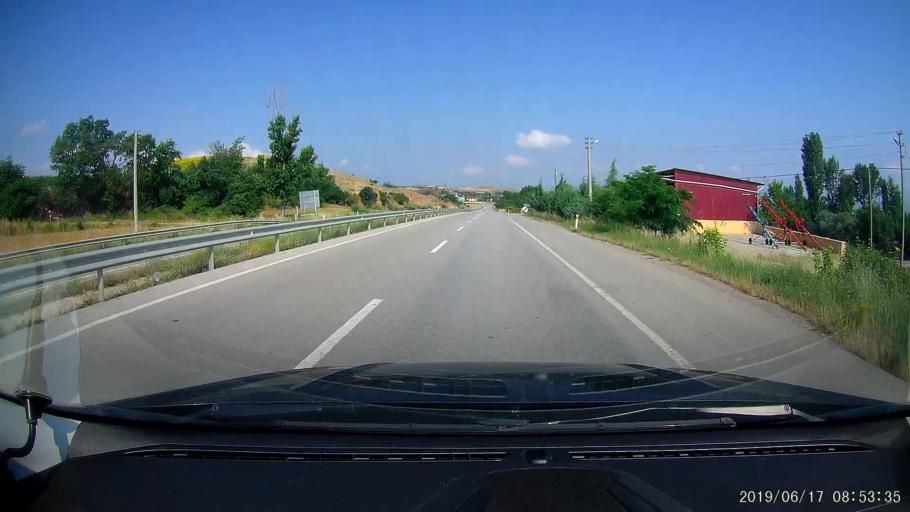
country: TR
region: Tokat
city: Erbaa
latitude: 40.7111
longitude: 36.4787
